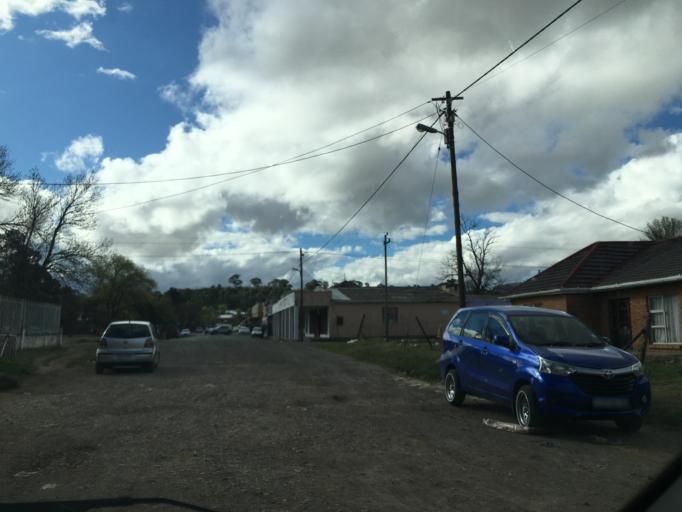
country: ZA
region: Eastern Cape
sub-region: Chris Hani District Municipality
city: Elliot
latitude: -31.3350
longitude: 27.8517
